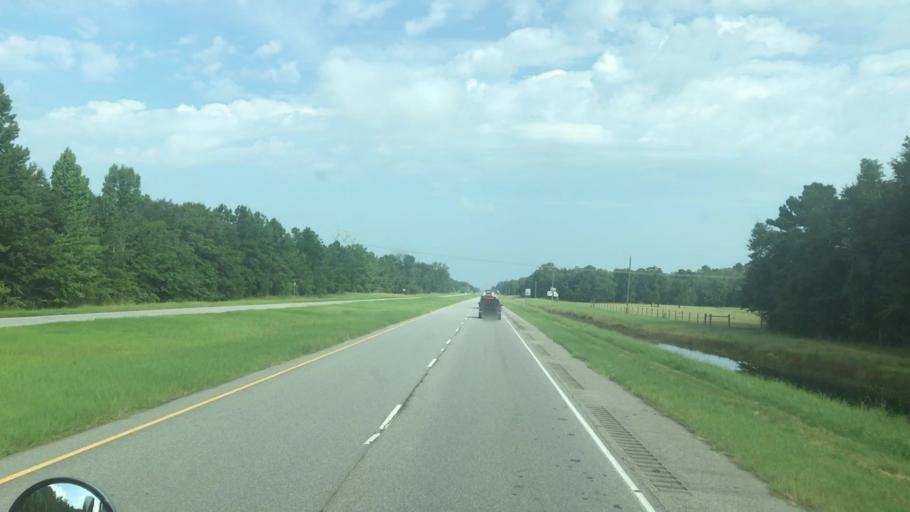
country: US
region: Georgia
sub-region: Early County
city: Blakely
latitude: 31.2822
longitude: -84.8393
